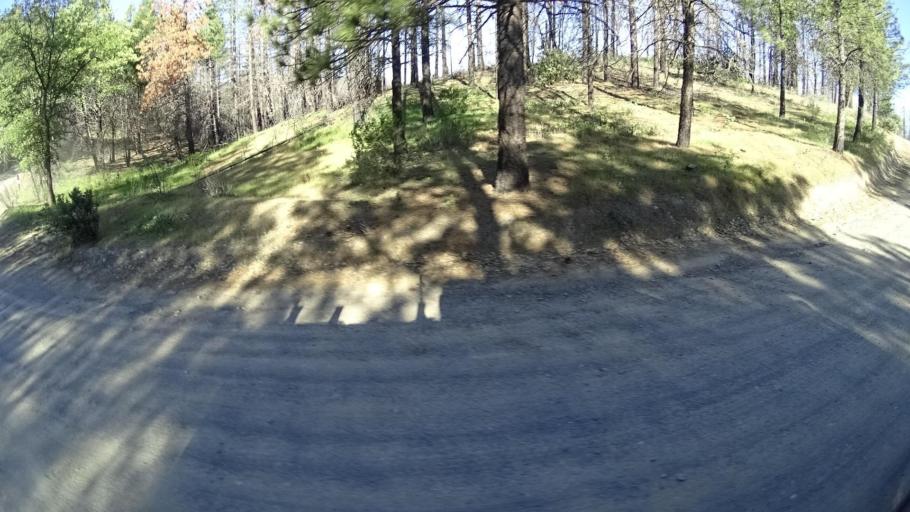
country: US
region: California
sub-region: Lake County
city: Upper Lake
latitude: 39.3358
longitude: -122.9560
